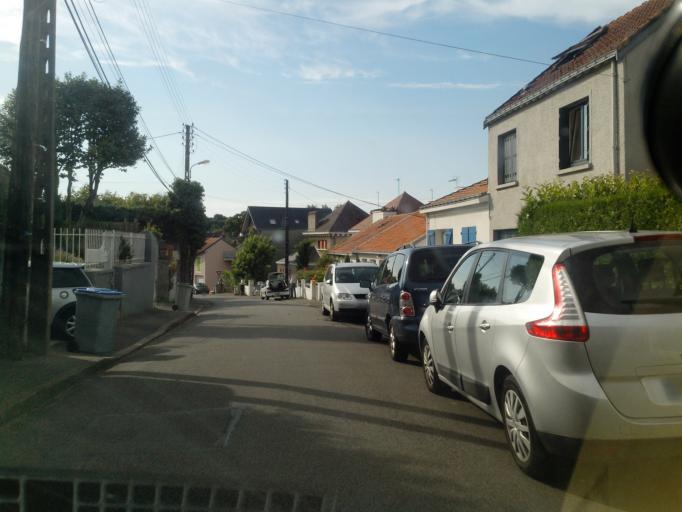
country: FR
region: Pays de la Loire
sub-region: Departement de la Loire-Atlantique
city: Nantes
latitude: 47.2511
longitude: -1.5785
